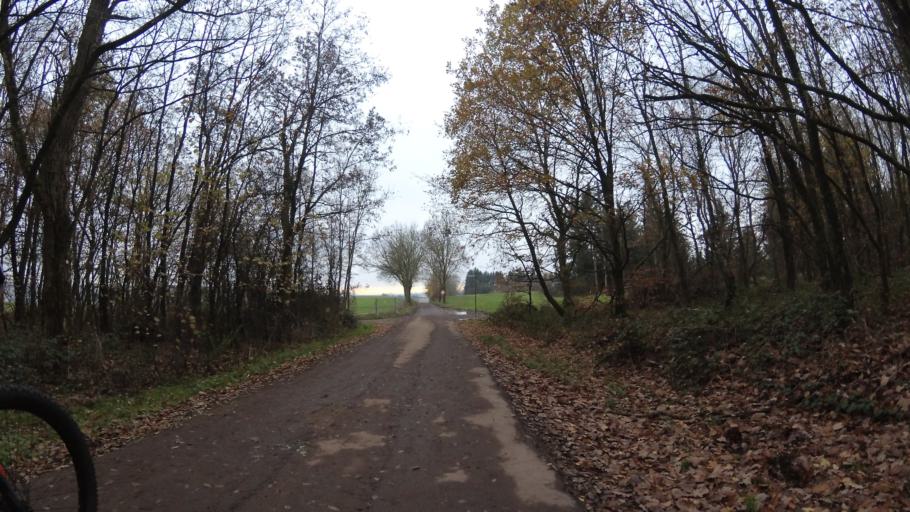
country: DE
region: Saarland
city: Illingen
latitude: 49.3979
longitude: 7.0652
